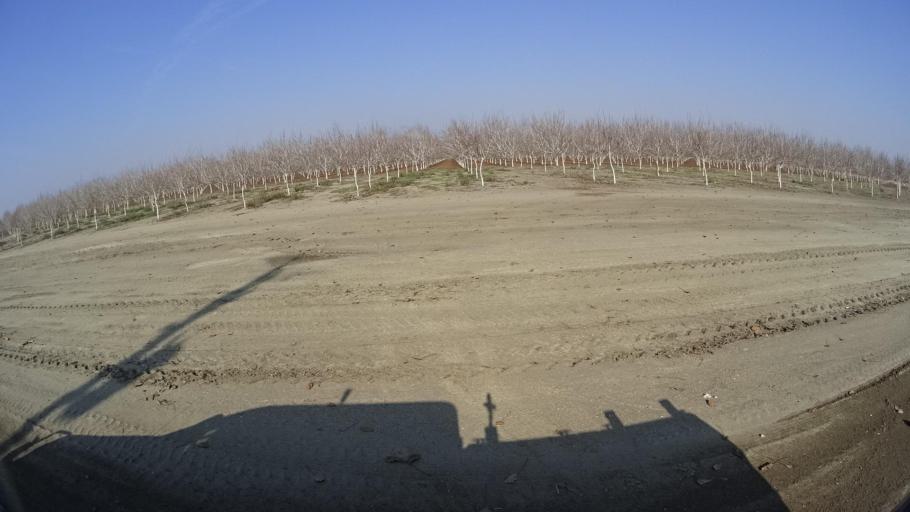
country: US
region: California
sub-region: Kern County
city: Buttonwillow
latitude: 35.3694
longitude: -119.4160
